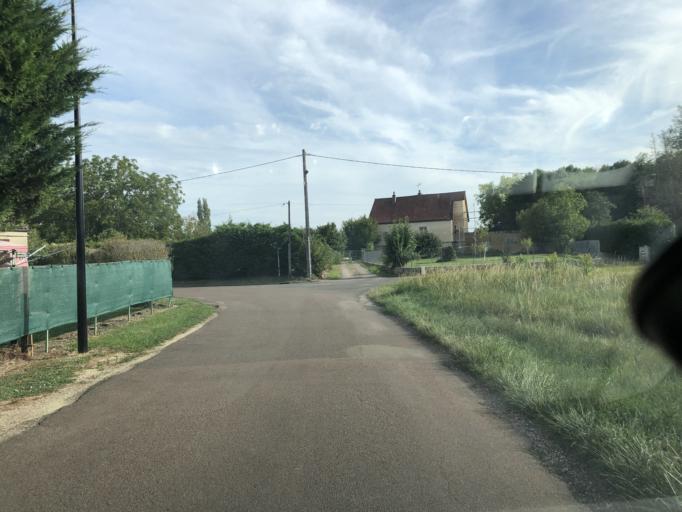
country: FR
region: Bourgogne
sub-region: Departement de l'Yonne
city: Aillant-sur-Tholon
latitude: 47.9231
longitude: 3.3636
